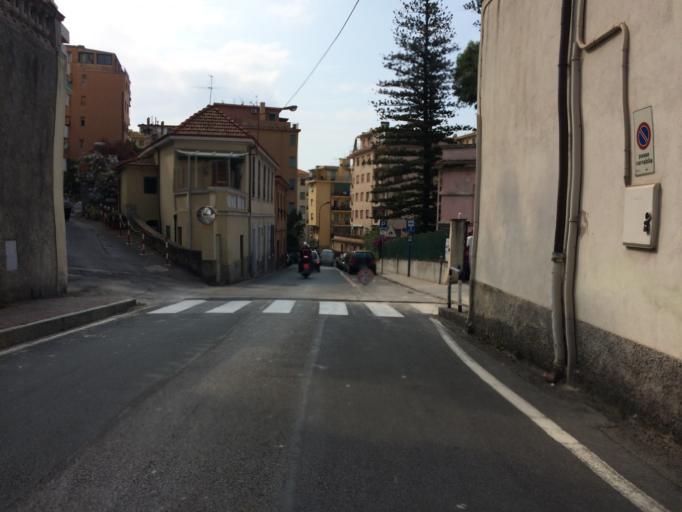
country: IT
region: Liguria
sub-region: Provincia di Imperia
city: San Remo
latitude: 43.8224
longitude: 7.7763
